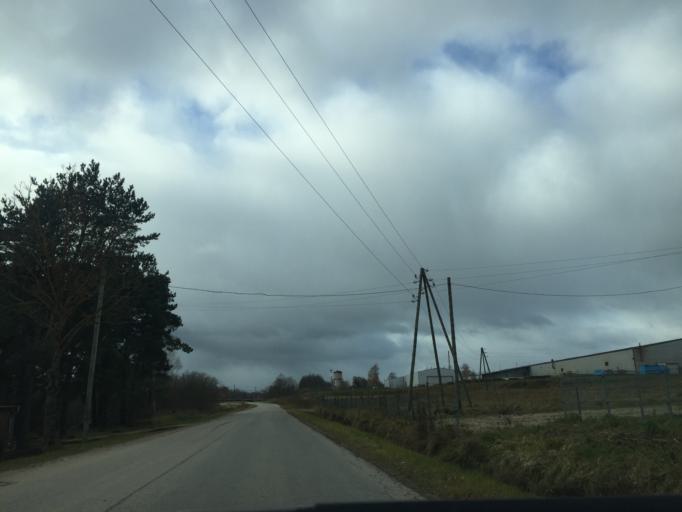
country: LV
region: Tukuma Rajons
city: Tukums
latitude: 56.9603
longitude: 23.1257
